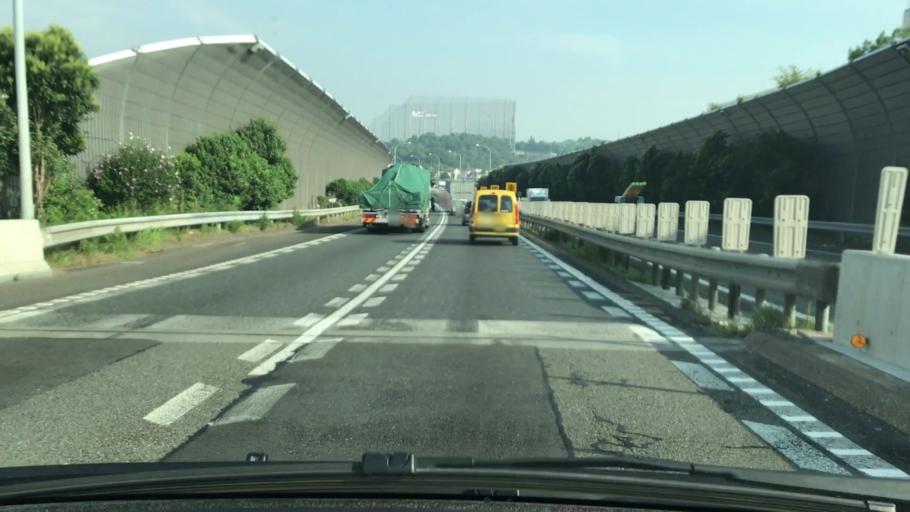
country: JP
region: Hyogo
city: Akashi
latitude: 34.6715
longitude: 135.0228
